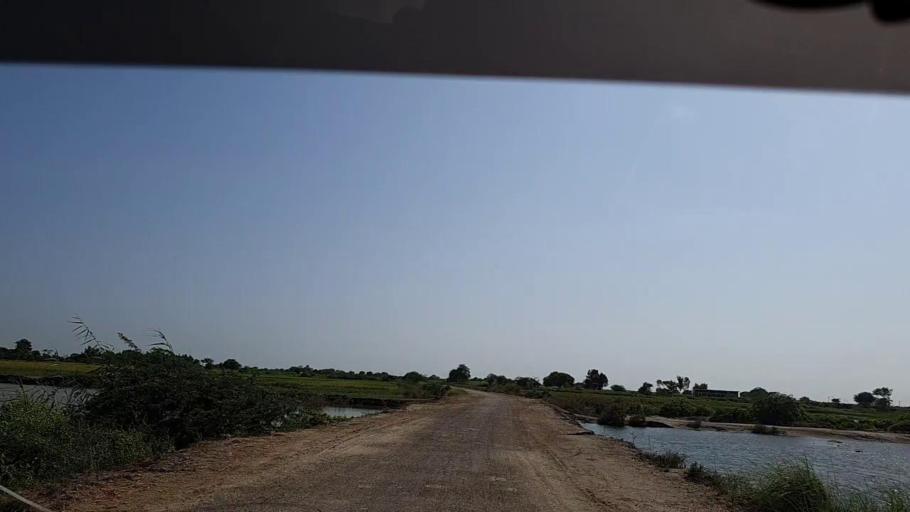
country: PK
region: Sindh
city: Badin
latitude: 24.6261
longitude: 68.7826
